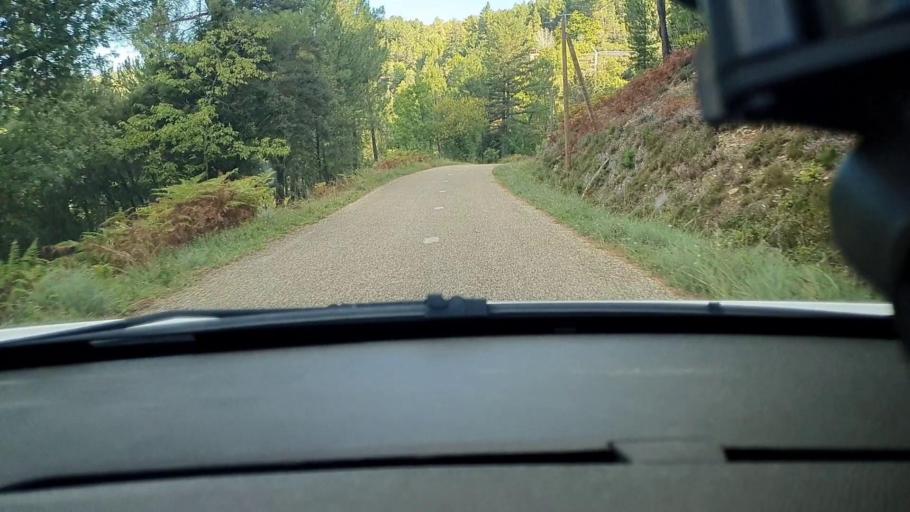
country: FR
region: Languedoc-Roussillon
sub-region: Departement du Gard
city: Besseges
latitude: 44.3313
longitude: 3.9990
